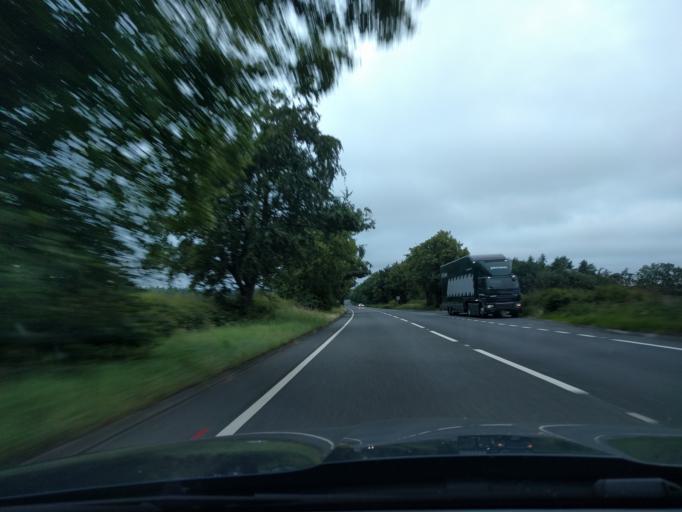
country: GB
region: England
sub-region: Northumberland
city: Hebron
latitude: 55.2105
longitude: -1.7102
